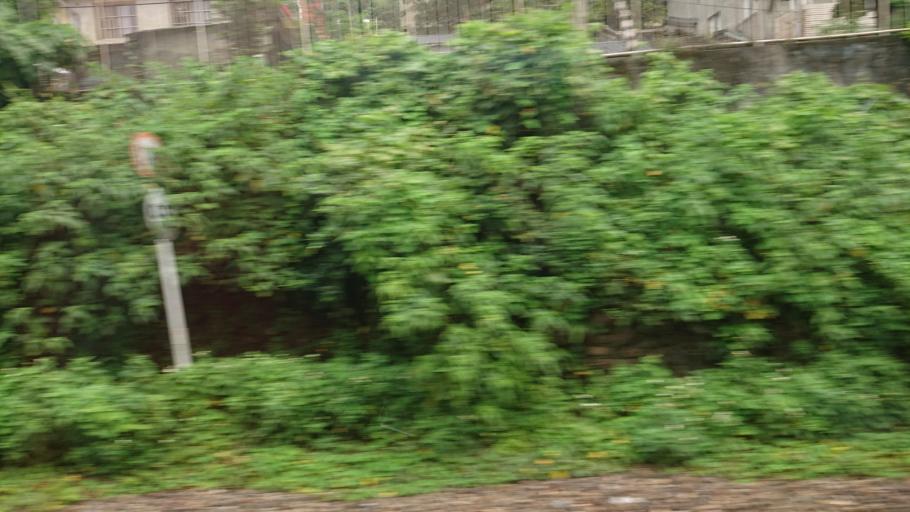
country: TW
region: Taiwan
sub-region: Yilan
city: Yilan
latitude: 24.9363
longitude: 121.8868
